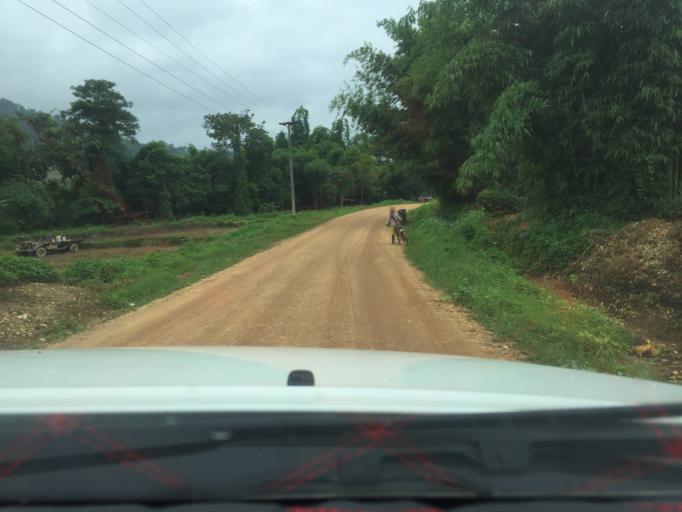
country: TH
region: Phayao
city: Phu Sang
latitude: 19.6791
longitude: 100.5035
